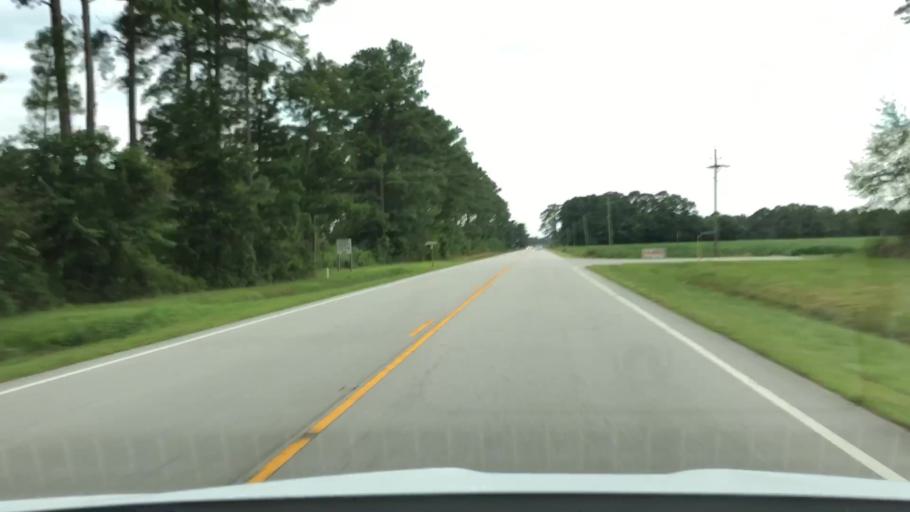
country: US
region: North Carolina
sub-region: Jones County
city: Trenton
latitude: 35.0742
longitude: -77.3861
